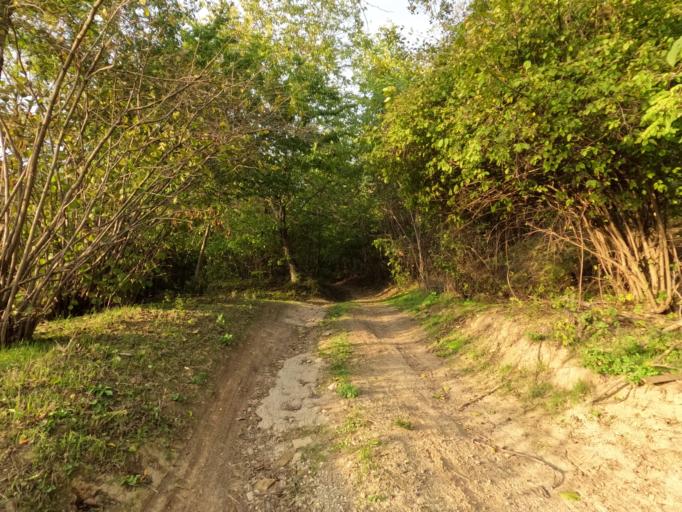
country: HU
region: Tolna
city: Szekszard
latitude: 46.3396
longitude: 18.6723
